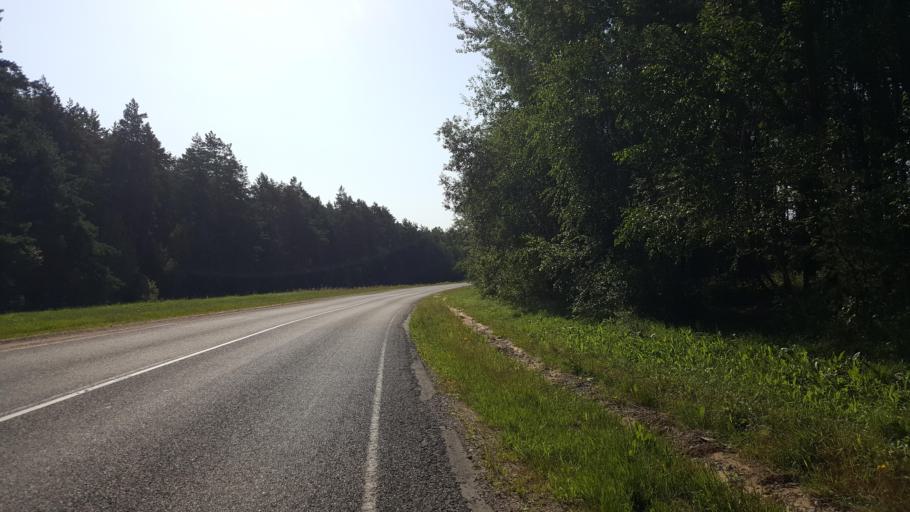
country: BY
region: Brest
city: Kamyanyets
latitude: 52.3848
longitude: 23.8566
